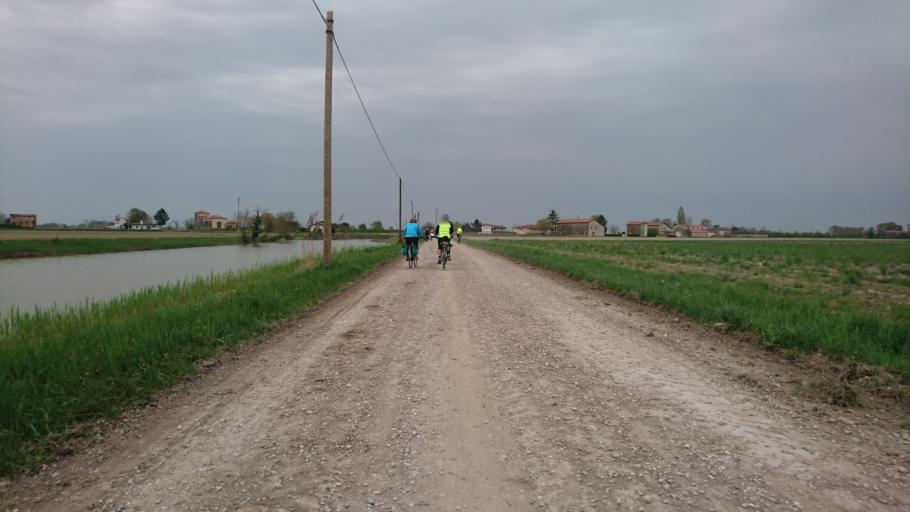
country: IT
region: Veneto
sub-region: Provincia di Venezia
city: Lugugnana
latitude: 45.6875
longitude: 12.9433
